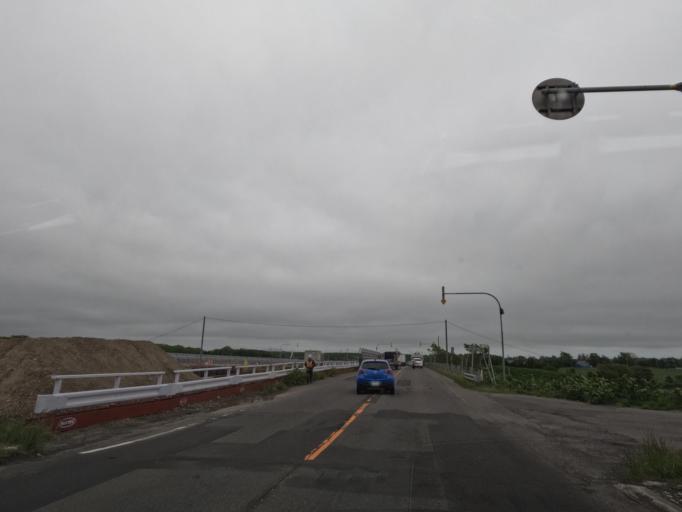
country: JP
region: Hokkaido
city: Ebetsu
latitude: 43.1392
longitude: 141.5136
